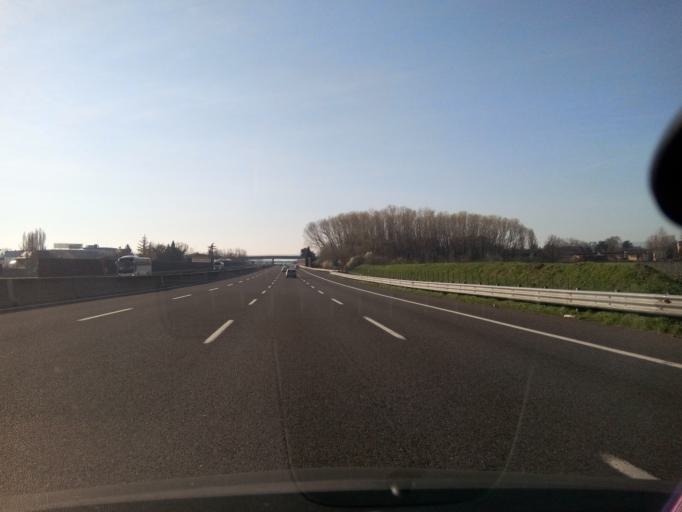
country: IT
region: Emilia-Romagna
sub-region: Provincia di Modena
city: Baggiovara
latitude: 44.6400
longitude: 10.8713
